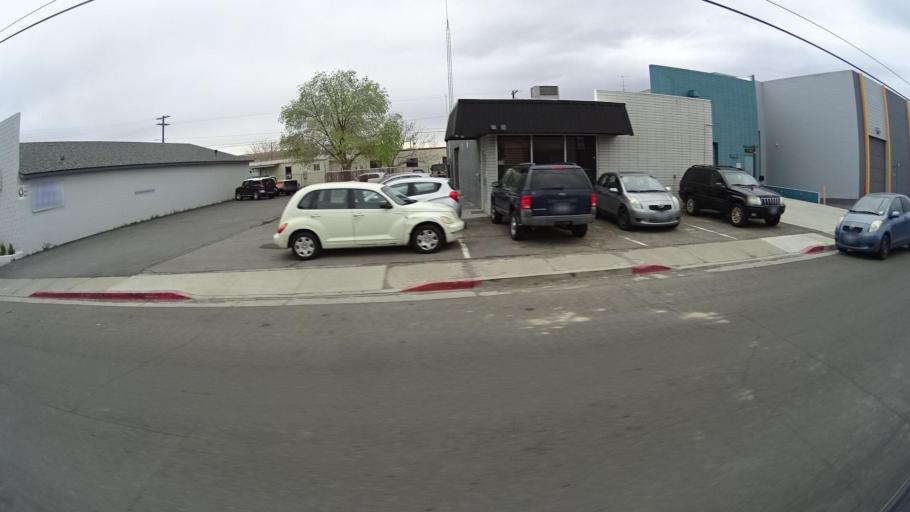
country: US
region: Nevada
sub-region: Washoe County
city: Reno
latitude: 39.5237
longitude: -119.7879
